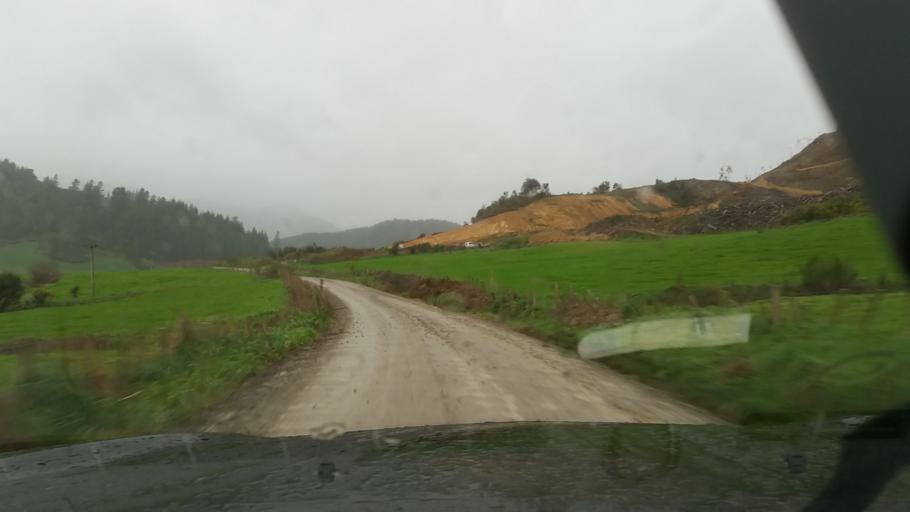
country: NZ
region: Marlborough
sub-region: Marlborough District
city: Picton
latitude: -41.3401
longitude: 173.9264
